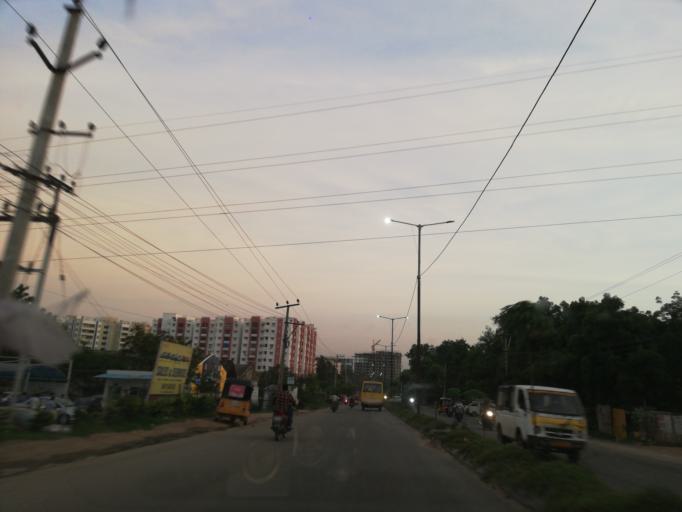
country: IN
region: Telangana
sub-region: Rangareddi
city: Kukatpalli
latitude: 17.5089
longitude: 78.3621
